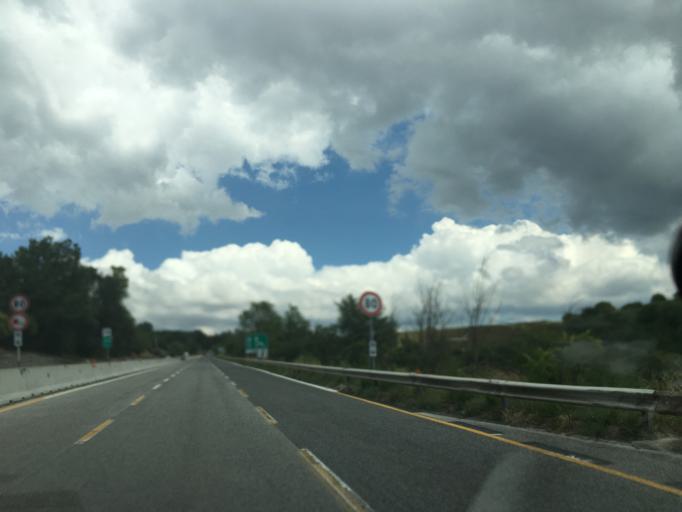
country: IT
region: Campania
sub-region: Provincia di Avellino
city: Bonito
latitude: 41.0728
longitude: 14.9811
